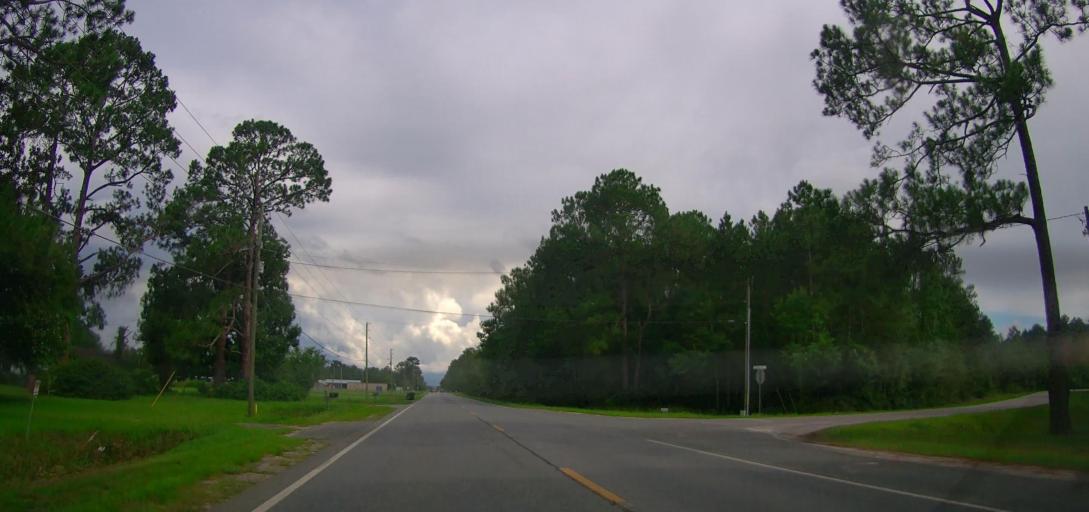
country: US
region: Georgia
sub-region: Wayne County
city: Jesup
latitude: 31.6377
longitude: -81.9042
